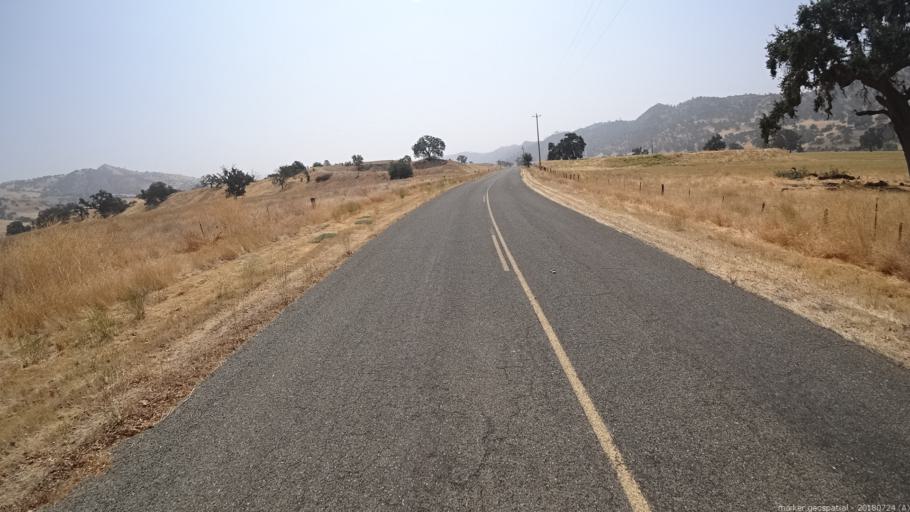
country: US
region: California
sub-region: Monterey County
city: King City
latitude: 36.1809
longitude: -120.7980
